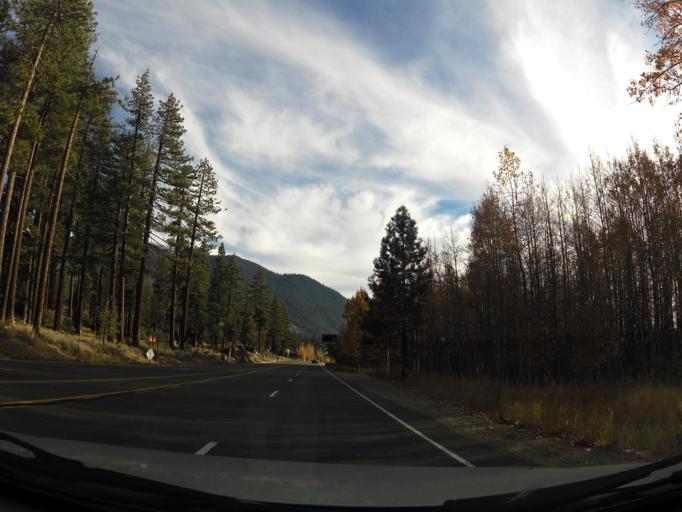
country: US
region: Nevada
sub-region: Douglas County
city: Kingsbury
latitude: 38.9745
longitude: -119.9356
